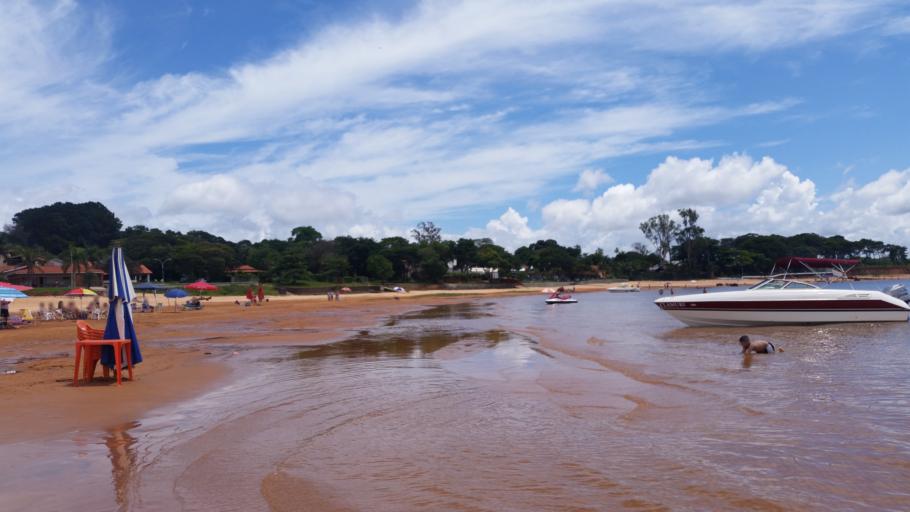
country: BR
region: Sao Paulo
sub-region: Itai
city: Itai
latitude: -23.2799
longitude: -49.0193
